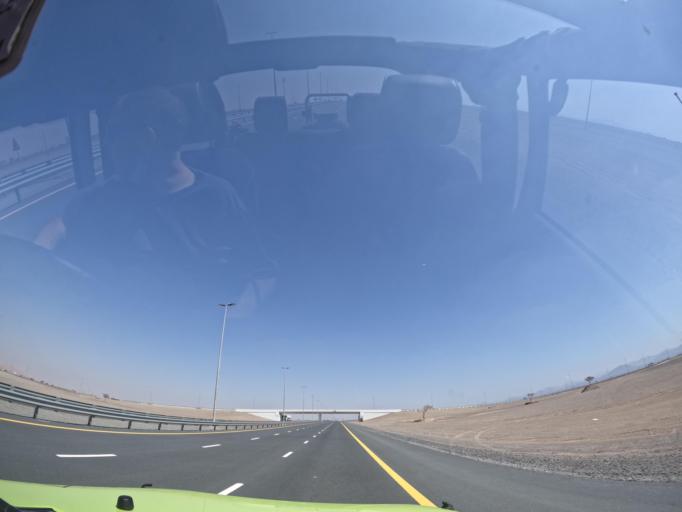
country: AE
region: Ash Shariqah
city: Adh Dhayd
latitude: 25.0452
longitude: 55.8923
